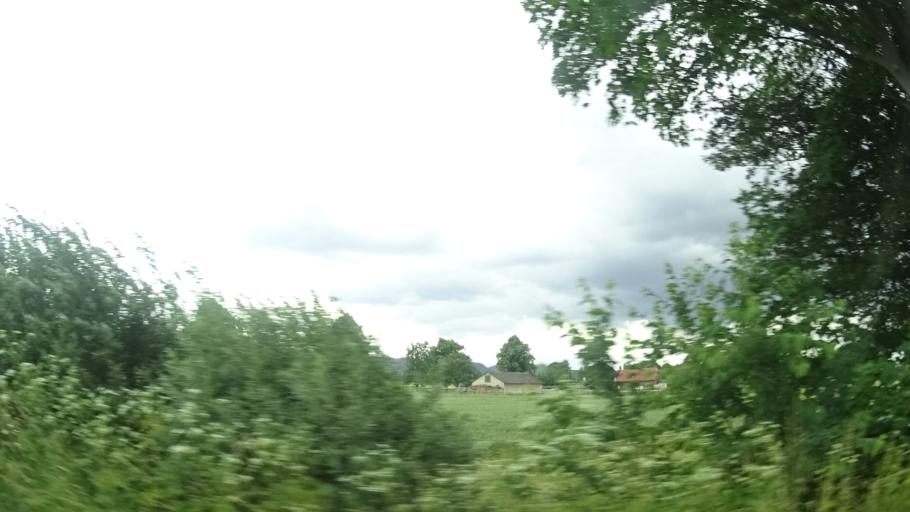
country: DE
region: Lower Saxony
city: Elze
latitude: 52.1617
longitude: 9.7127
